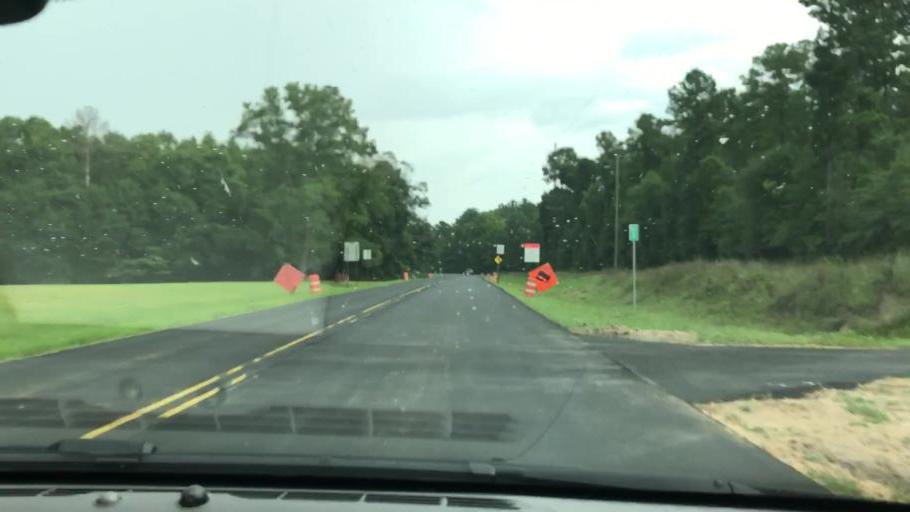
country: US
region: Georgia
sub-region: Clay County
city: Fort Gaines
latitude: 31.5270
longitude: -85.0233
